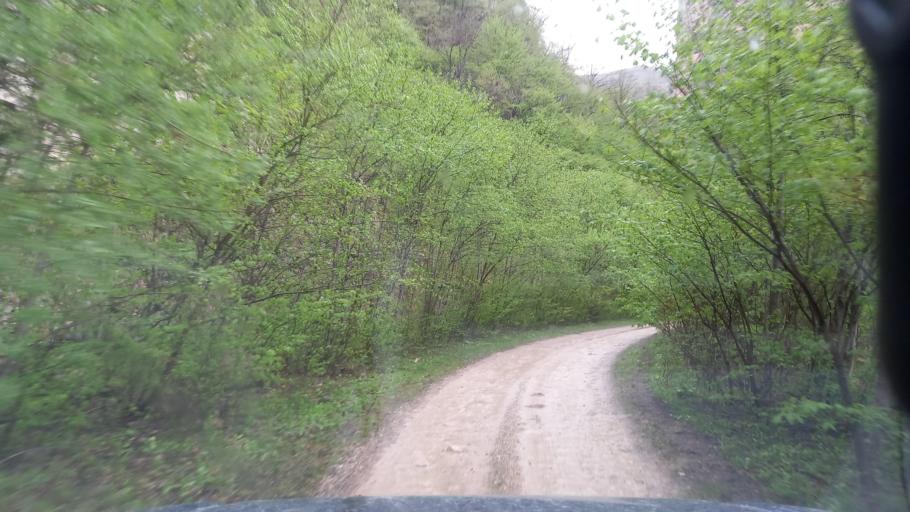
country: RU
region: Kabardino-Balkariya
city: Bylym
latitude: 43.5873
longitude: 43.0210
